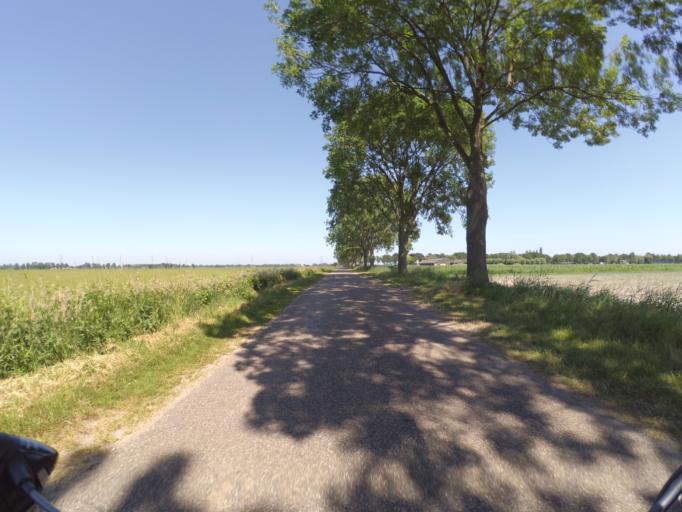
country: NL
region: North Brabant
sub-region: Gemeente Dongen
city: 's Gravenmoer
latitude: 51.6484
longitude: 4.9665
